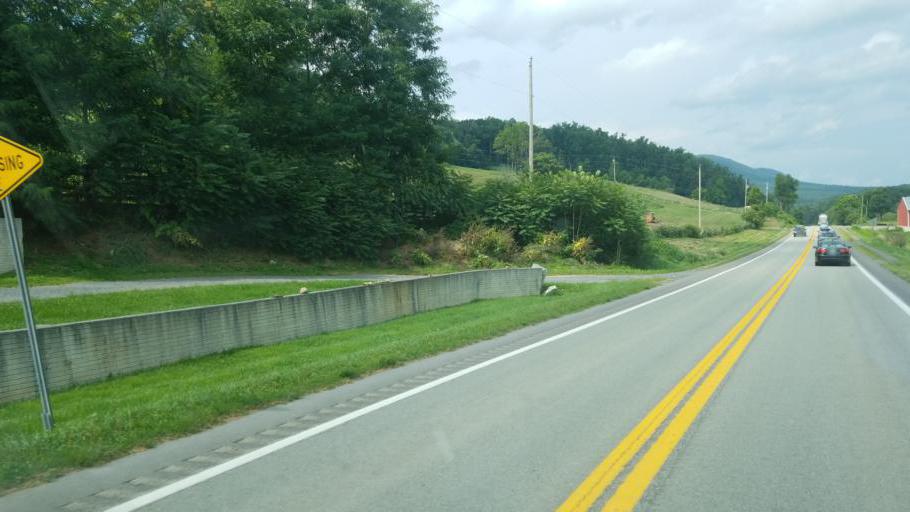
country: US
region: Virginia
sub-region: Frederick County
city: Shawnee Land
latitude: 39.3689
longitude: -78.3730
